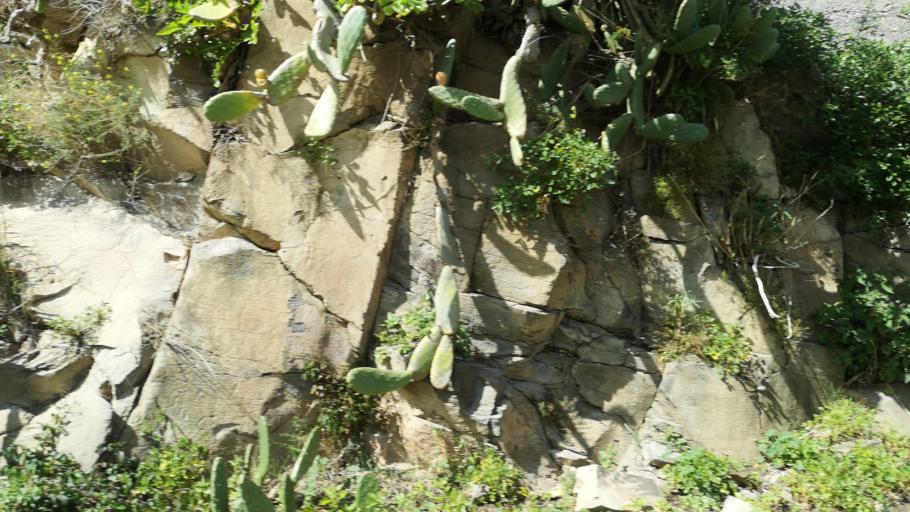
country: ES
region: Canary Islands
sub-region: Provincia de Santa Cruz de Tenerife
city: Vallehermosa
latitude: 28.1363
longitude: -17.3162
